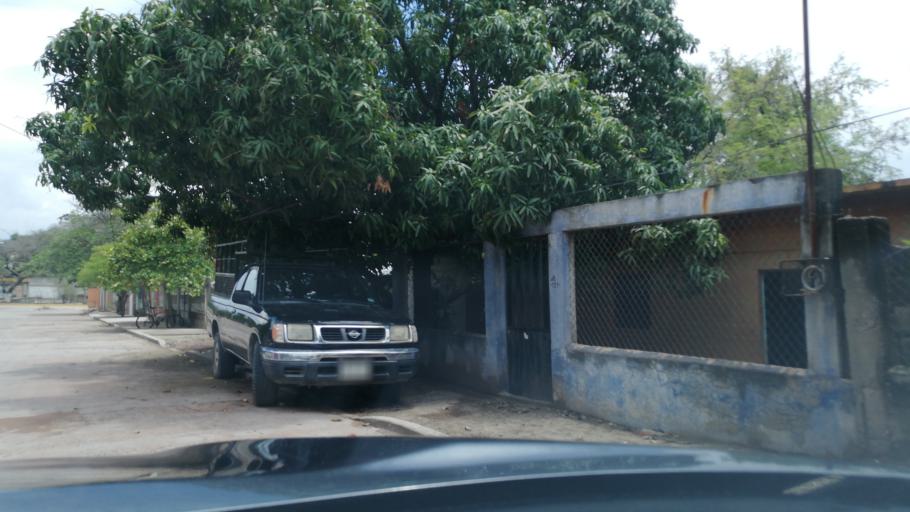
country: MX
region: Oaxaca
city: Santa Maria Jalapa del Marques
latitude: 16.4439
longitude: -95.4418
